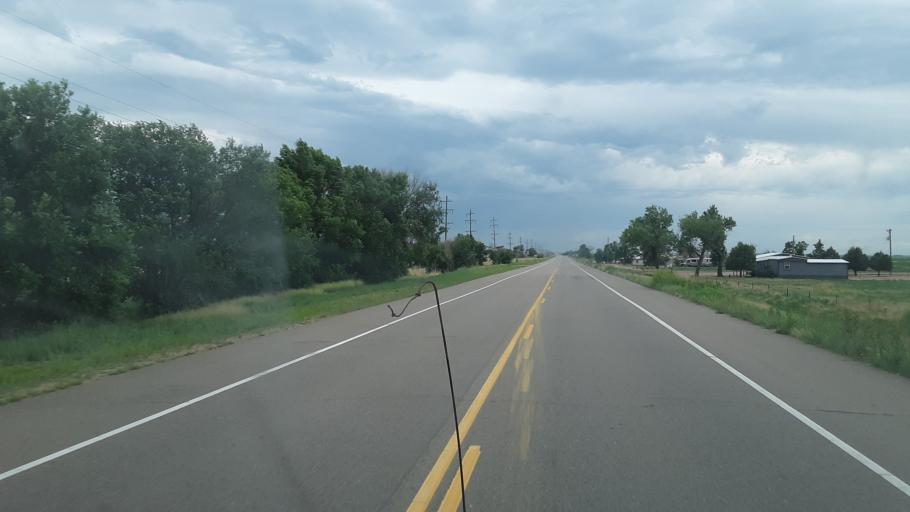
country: US
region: Colorado
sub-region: Crowley County
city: Ordway
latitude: 38.2084
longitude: -103.7482
